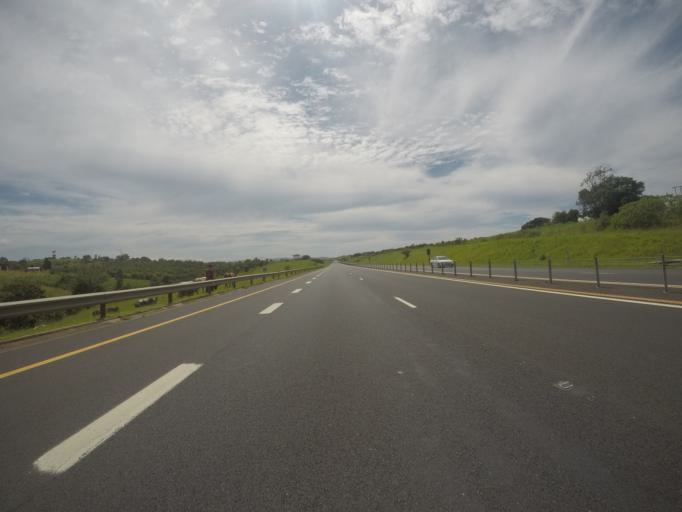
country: ZA
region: KwaZulu-Natal
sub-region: iLembe District Municipality
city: Mandeni
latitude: -29.1822
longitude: 31.4895
